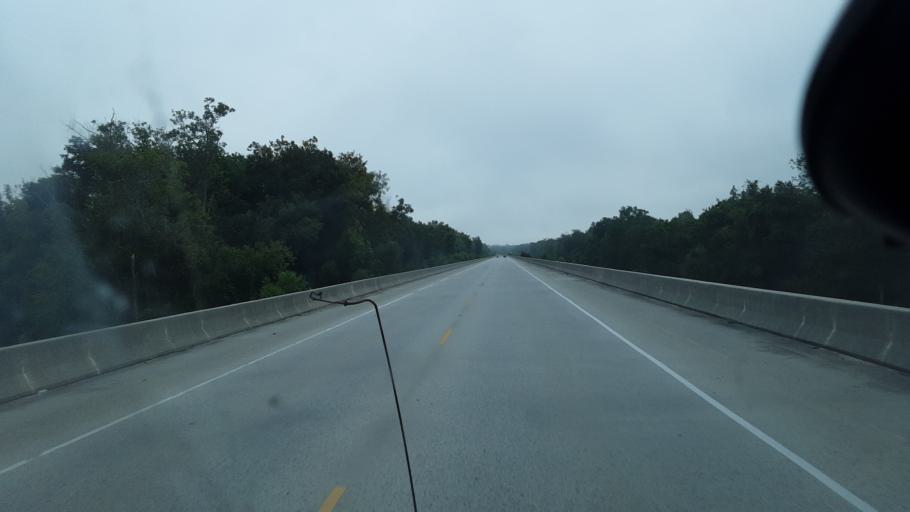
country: US
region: South Carolina
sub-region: Florence County
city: Johnsonville
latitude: 33.9035
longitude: -79.4359
